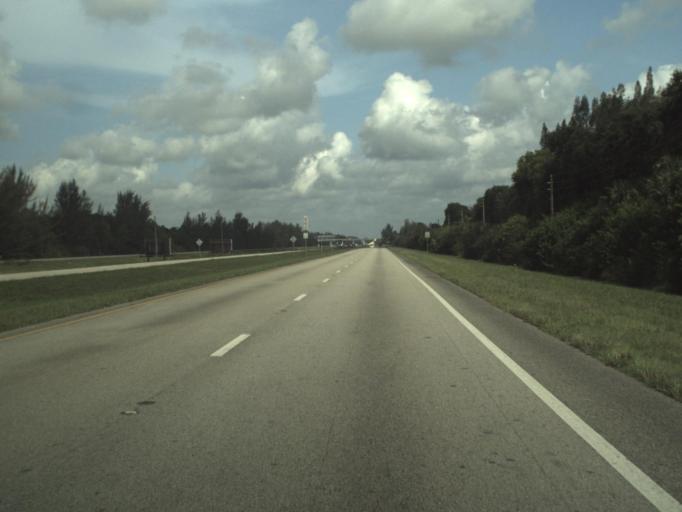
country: US
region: Florida
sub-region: Palm Beach County
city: Palm Beach Gardens
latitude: 26.7889
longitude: -80.1207
